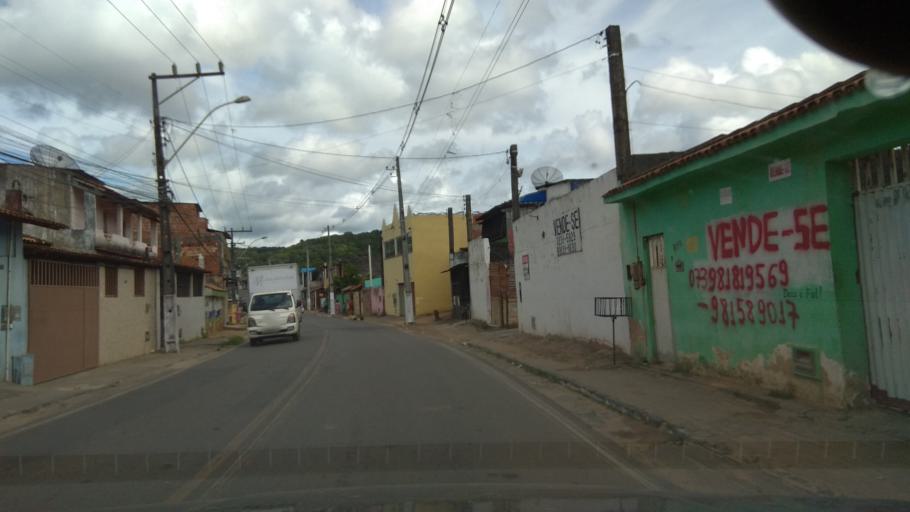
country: BR
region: Bahia
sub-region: Ilheus
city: Ilheus
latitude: -14.7843
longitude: -39.0574
